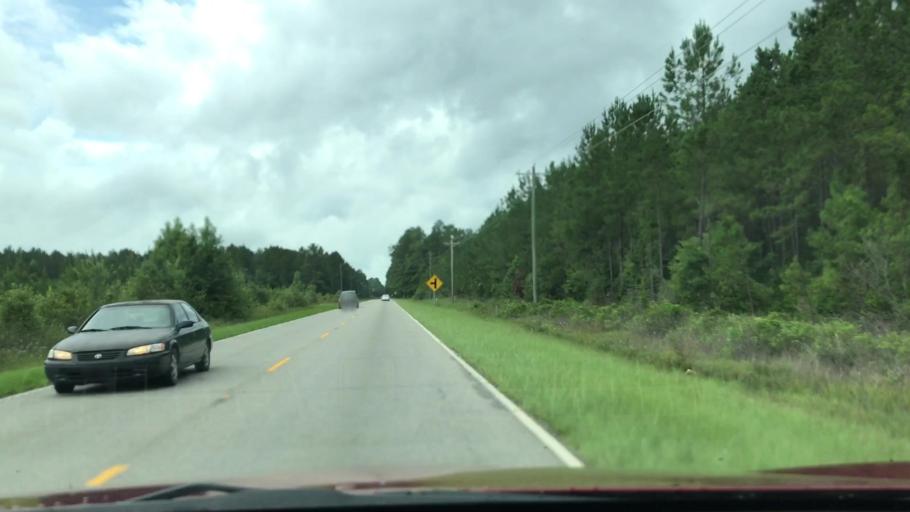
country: US
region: South Carolina
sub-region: Georgetown County
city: Murrells Inlet
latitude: 33.5698
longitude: -79.2114
